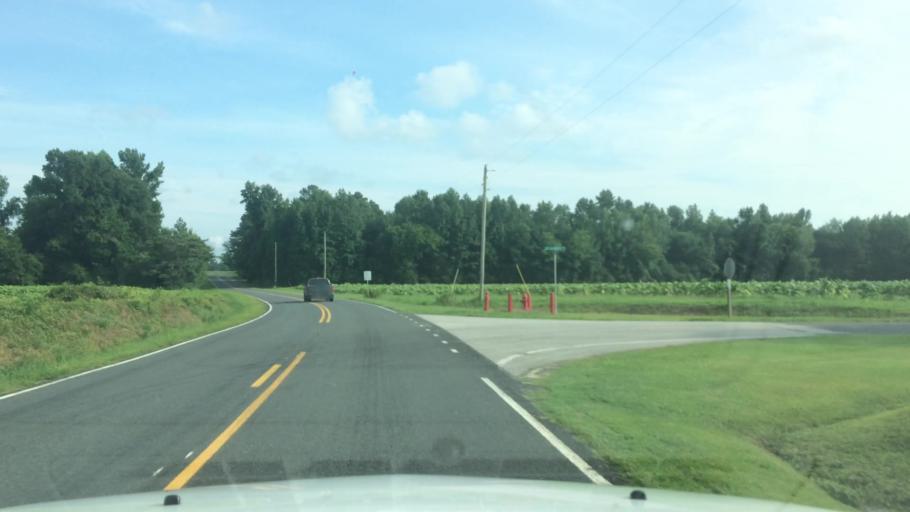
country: US
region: North Carolina
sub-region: Greene County
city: Maury
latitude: 35.4879
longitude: -77.5199
